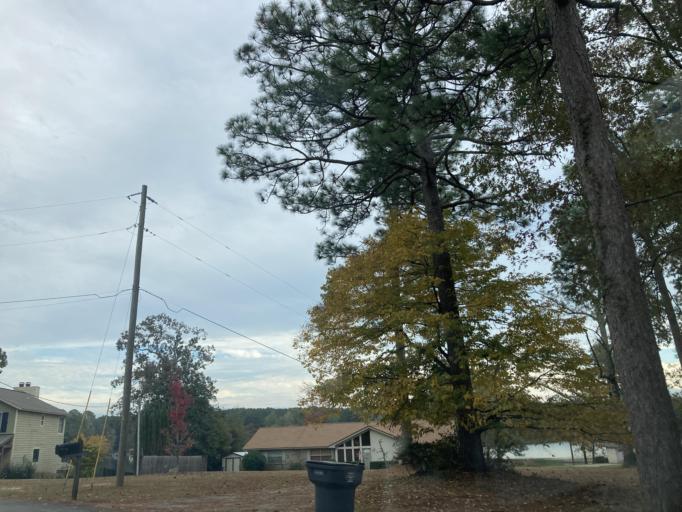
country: US
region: Mississippi
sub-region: Lamar County
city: West Hattiesburg
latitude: 31.2954
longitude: -89.4292
